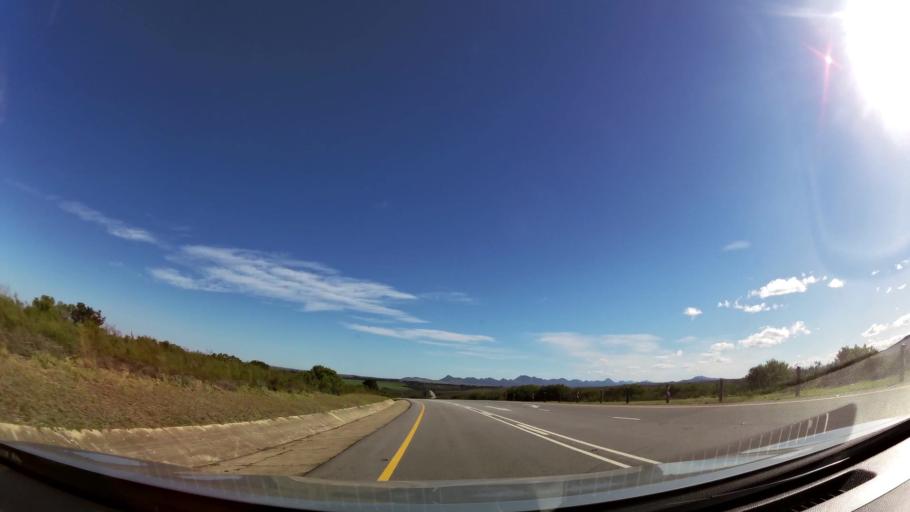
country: ZA
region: Eastern Cape
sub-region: Cacadu District Municipality
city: Kruisfontein
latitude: -34.0103
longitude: 24.6511
